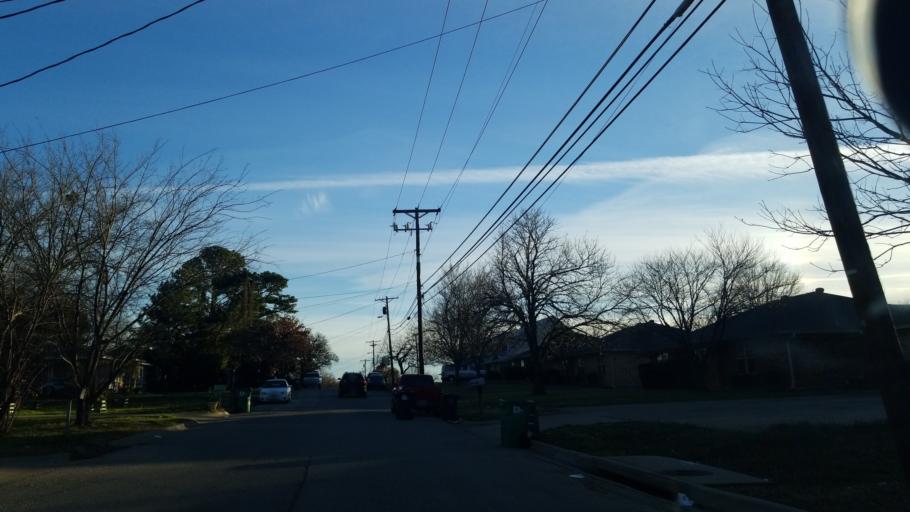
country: US
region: Texas
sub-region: Denton County
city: Denton
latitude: 33.1921
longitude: -97.1418
